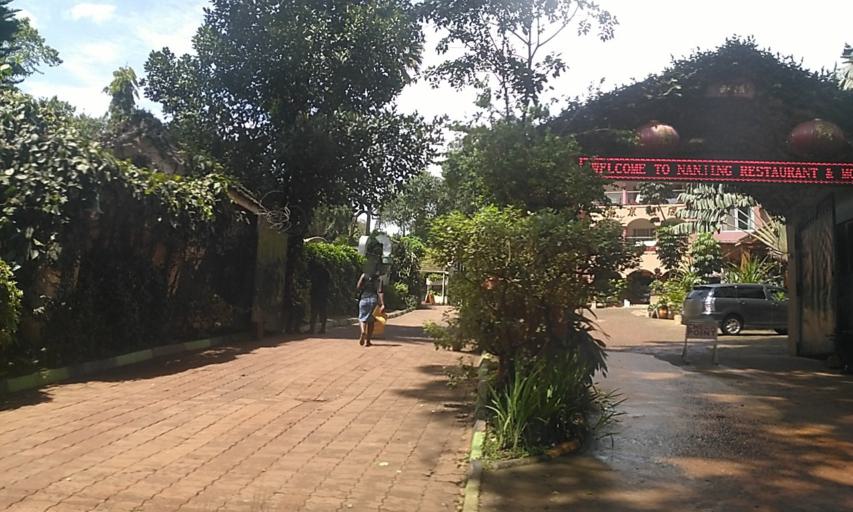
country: UG
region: Central Region
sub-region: Kampala District
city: Kampala
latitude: 0.3284
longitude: 32.5989
